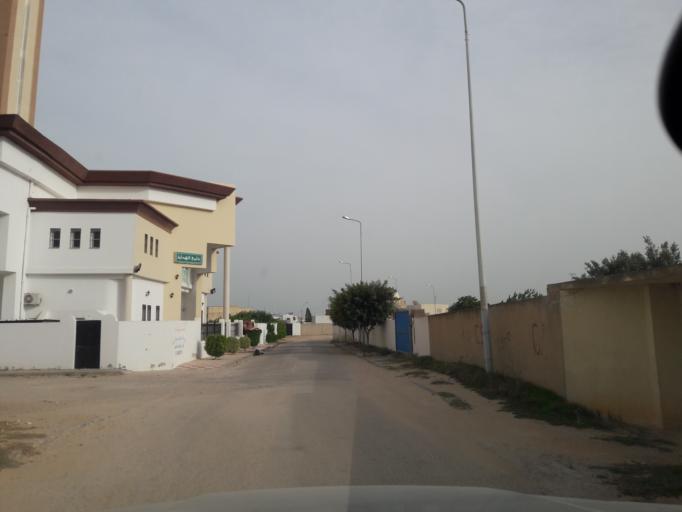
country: TN
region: Safaqis
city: Al Qarmadah
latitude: 34.7791
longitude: 10.7685
